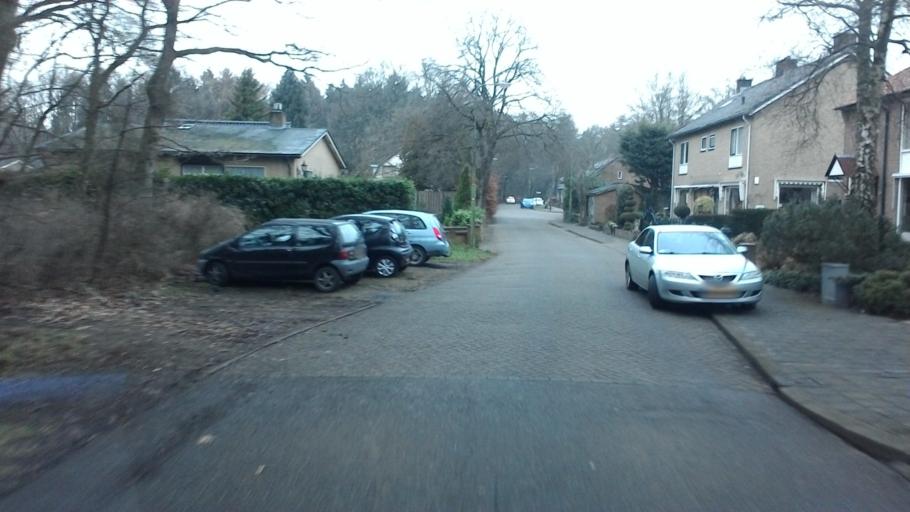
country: NL
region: Utrecht
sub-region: Gemeente Utrechtse Heuvelrug
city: Driebergen-Rijsenburg
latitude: 52.0774
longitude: 5.3123
